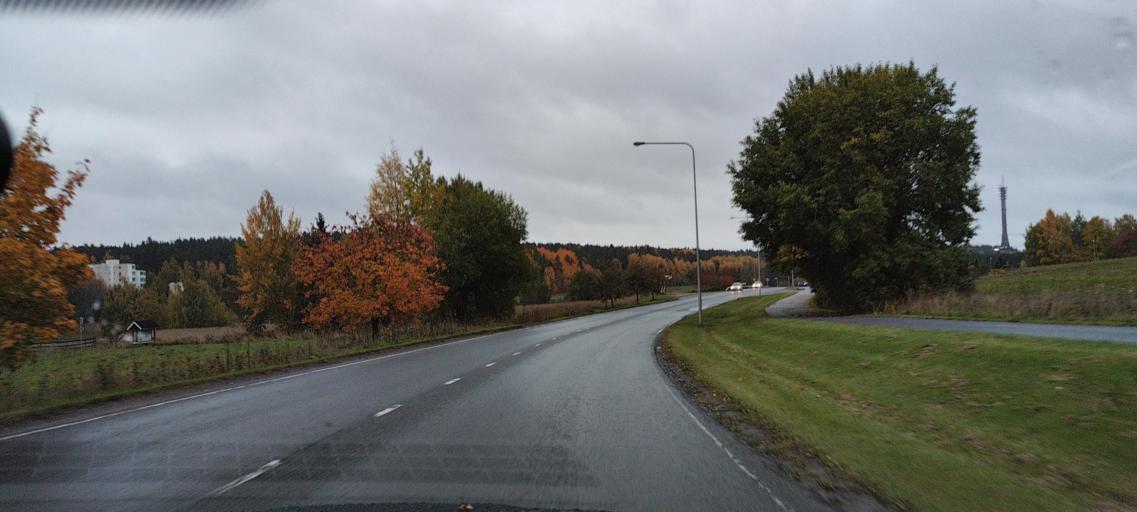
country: FI
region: Varsinais-Suomi
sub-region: Turku
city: Kaarina
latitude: 60.4602
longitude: 22.3349
